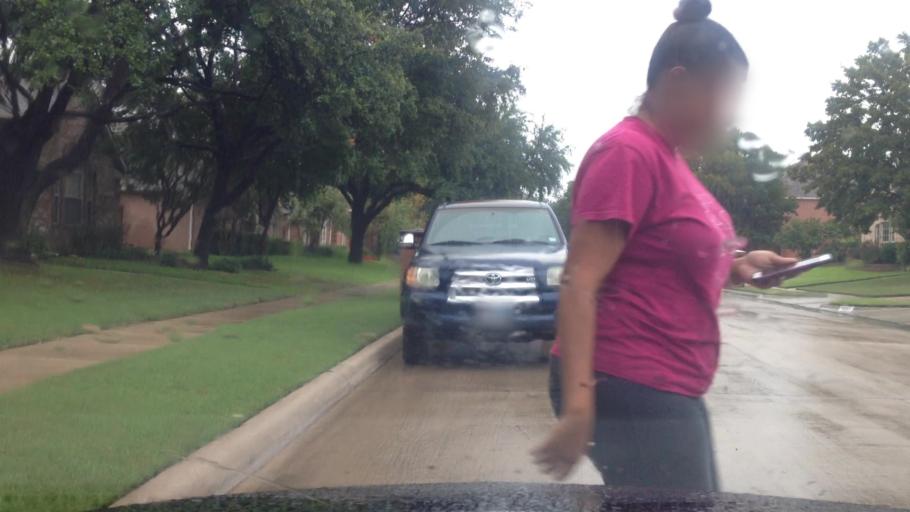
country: US
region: Texas
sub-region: Tarrant County
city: Keller
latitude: 32.9058
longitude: -97.2341
